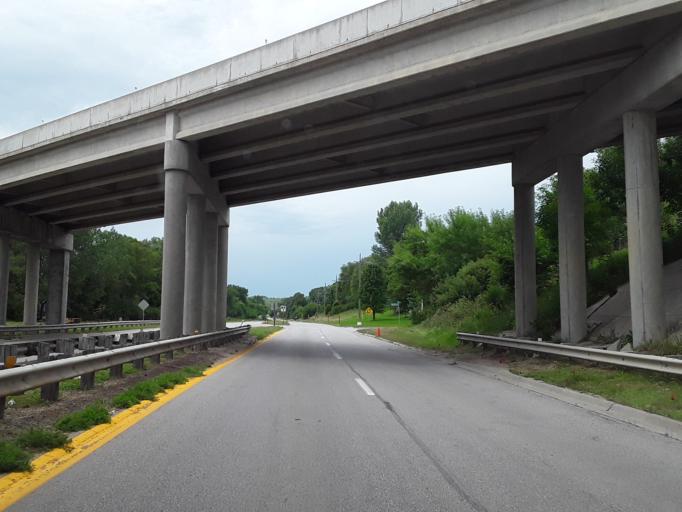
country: US
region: Iowa
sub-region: Pottawattamie County
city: Carter Lake
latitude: 41.3468
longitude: -95.9931
